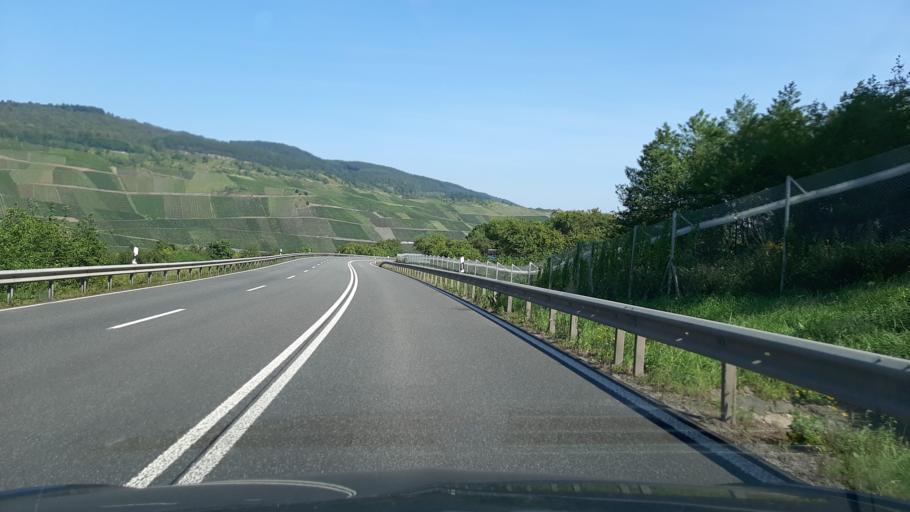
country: DE
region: Rheinland-Pfalz
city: Losnich
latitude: 49.9712
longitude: 7.0266
